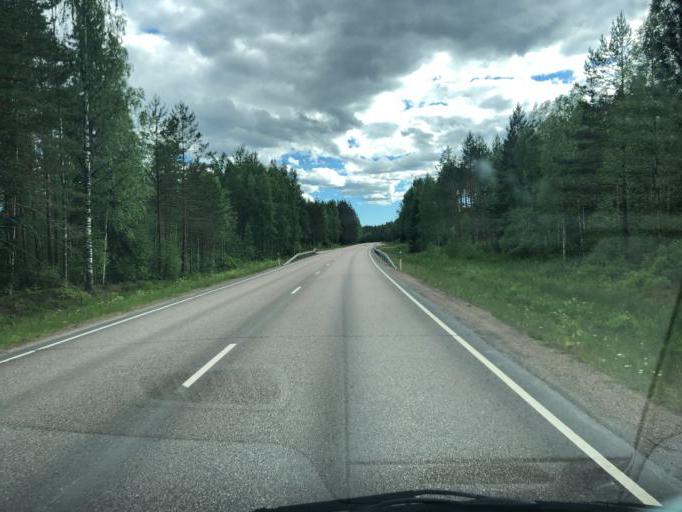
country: FI
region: Southern Savonia
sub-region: Mikkeli
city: Maentyharju
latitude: 61.1243
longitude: 27.1016
